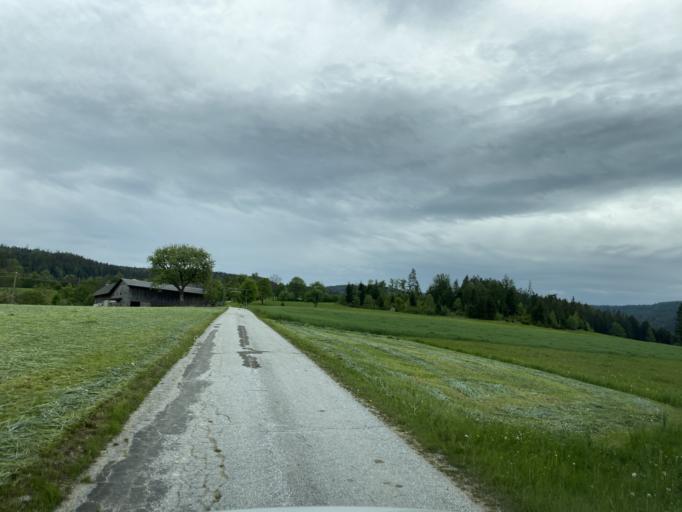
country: AT
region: Styria
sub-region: Politischer Bezirk Weiz
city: Gschaid bei Birkfeld
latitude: 47.3366
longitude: 15.7205
